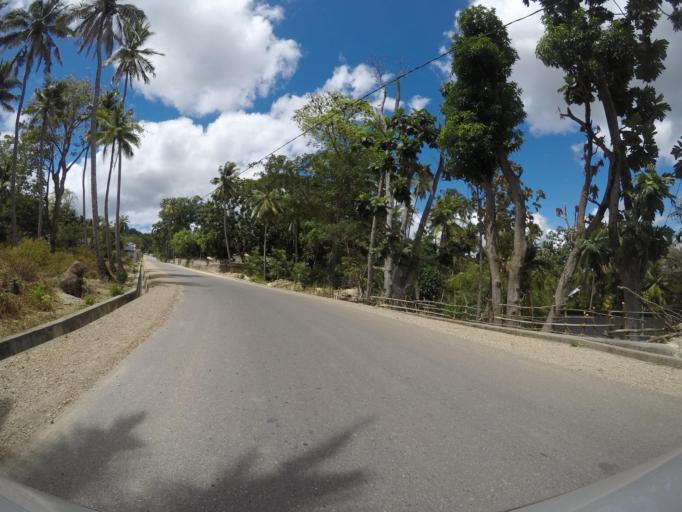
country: TL
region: Lautem
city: Lospalos
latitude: -8.3583
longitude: 126.9297
